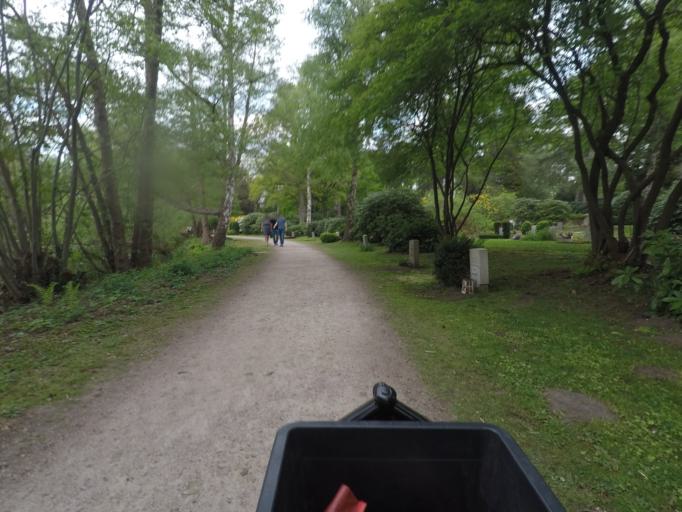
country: DE
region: Hamburg
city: Wellingsbuettel
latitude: 53.6285
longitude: 10.0681
